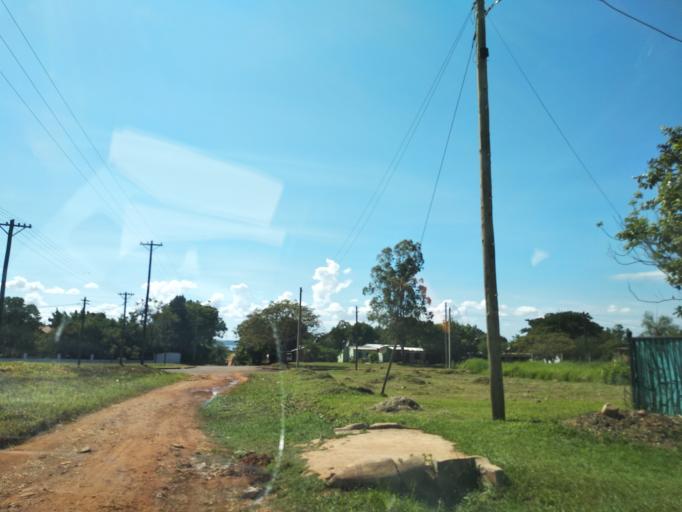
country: AR
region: Misiones
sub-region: Departamento de Capital
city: Posadas
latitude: -27.4259
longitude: -55.8823
